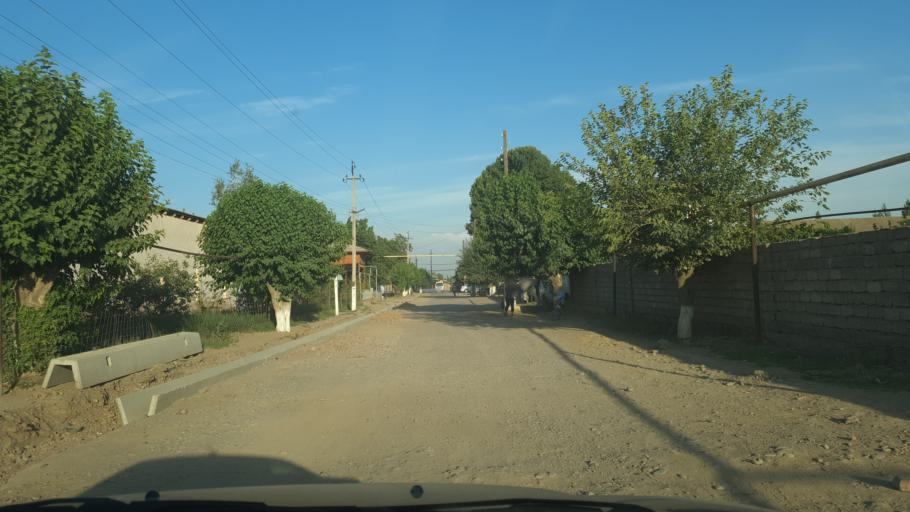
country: UZ
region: Toshkent
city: Tuytepa
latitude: 41.1038
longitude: 69.3995
